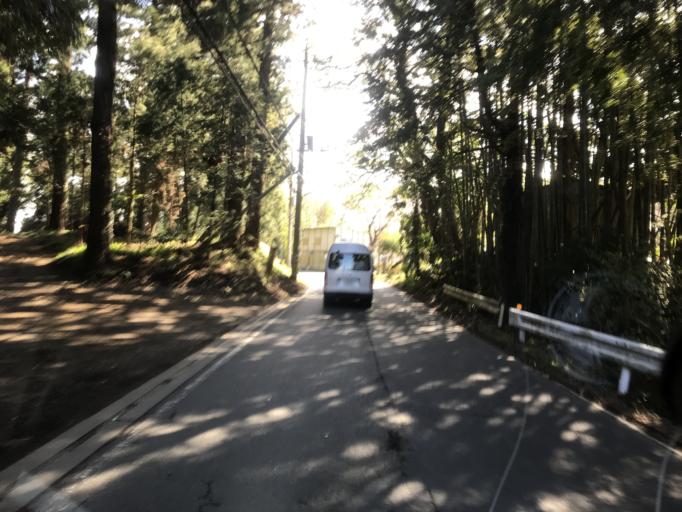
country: JP
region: Chiba
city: Sawara
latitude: 35.8398
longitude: 140.4291
